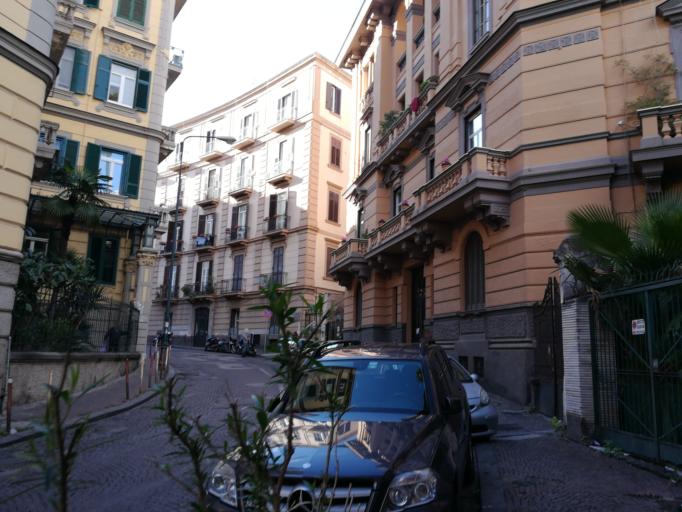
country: IT
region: Campania
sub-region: Provincia di Napoli
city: Napoli
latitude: 40.8386
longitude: 14.2374
